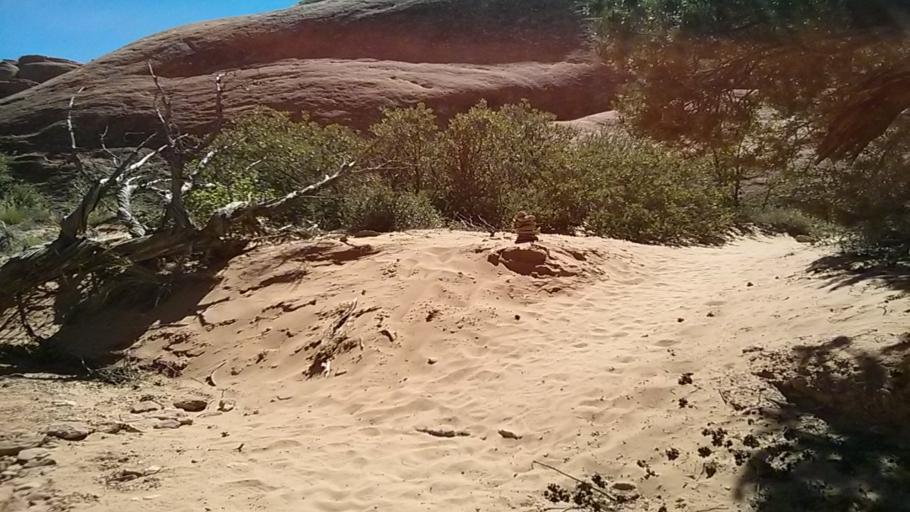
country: US
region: Utah
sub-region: Grand County
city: Moab
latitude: 38.8011
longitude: -109.6125
